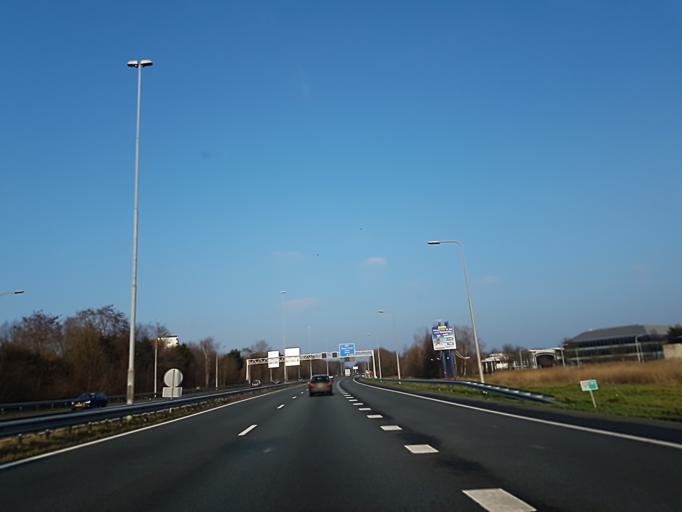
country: NL
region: North Brabant
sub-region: Gemeente Breda
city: Hoge Vucht
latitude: 51.5863
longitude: 4.8250
